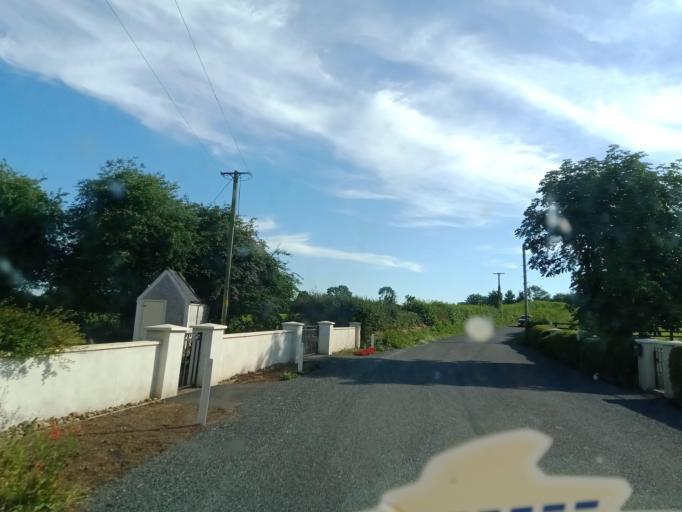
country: IE
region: Leinster
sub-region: Kilkenny
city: Ballyragget
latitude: 52.7731
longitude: -7.3882
